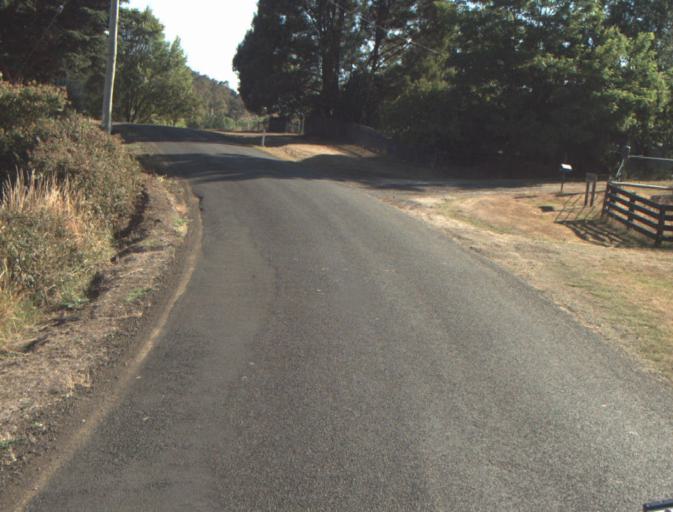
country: AU
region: Tasmania
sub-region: Launceston
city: Mayfield
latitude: -41.2946
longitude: 147.2036
